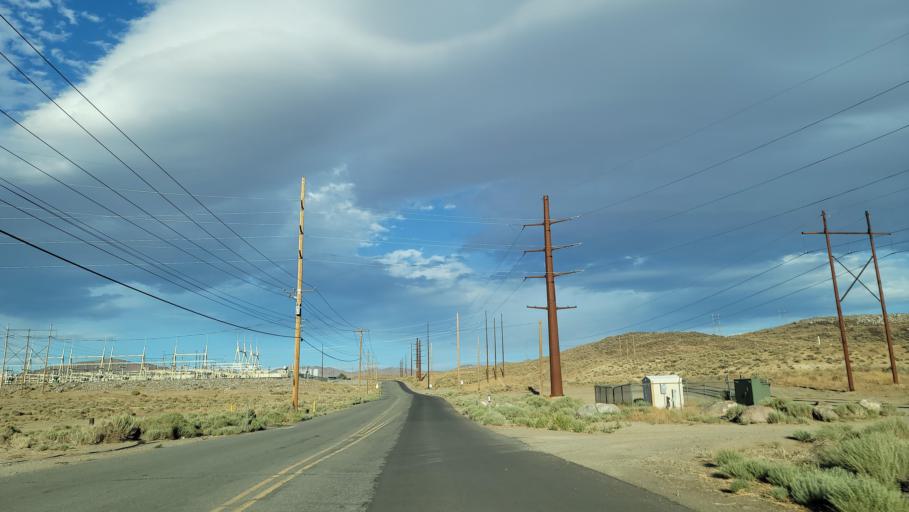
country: US
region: Nevada
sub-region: Washoe County
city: Spanish Springs
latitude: 39.5596
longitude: -119.5171
